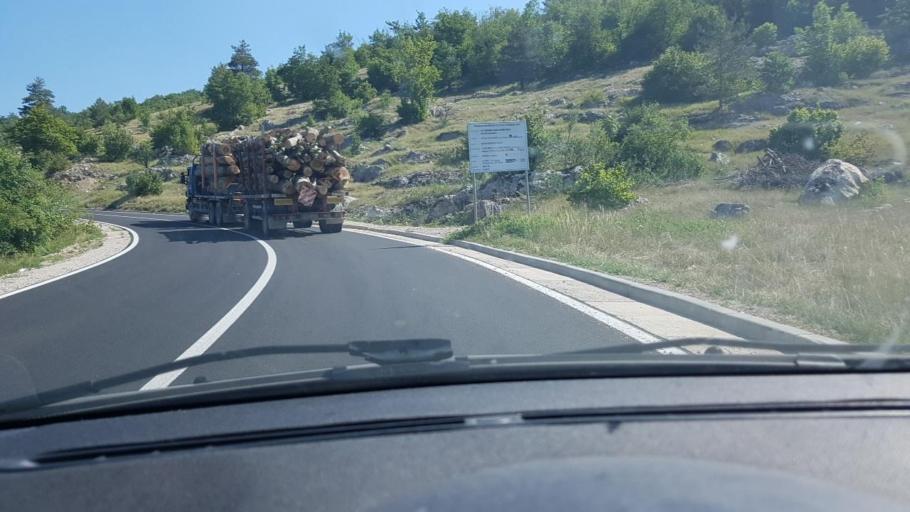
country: BA
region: Federation of Bosnia and Herzegovina
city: Bosansko Grahovo
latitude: 44.2999
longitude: 16.3070
